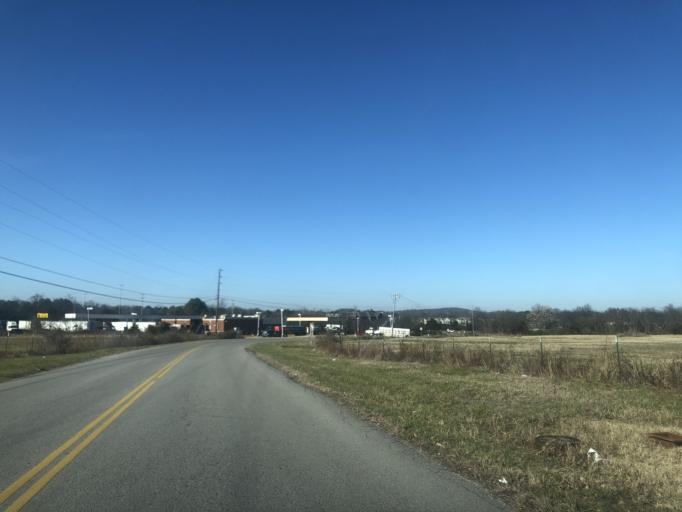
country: US
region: Tennessee
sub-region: Rutherford County
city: Smyrna
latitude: 35.9344
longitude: -86.5278
